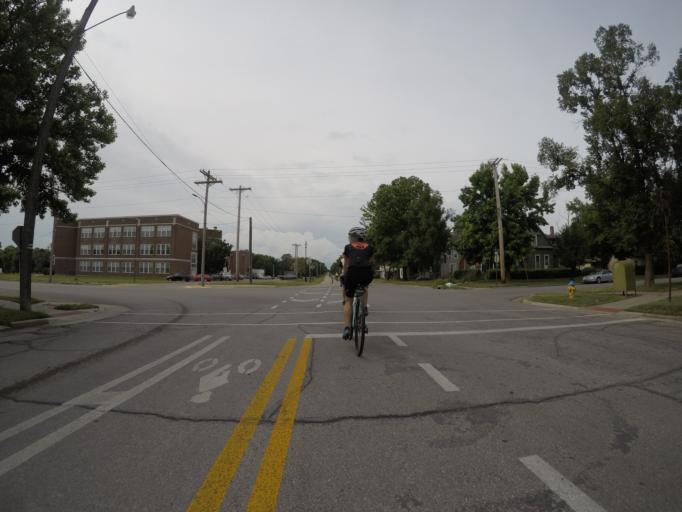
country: US
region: Kansas
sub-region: Franklin County
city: Ottawa
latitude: 38.6115
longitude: -95.2700
